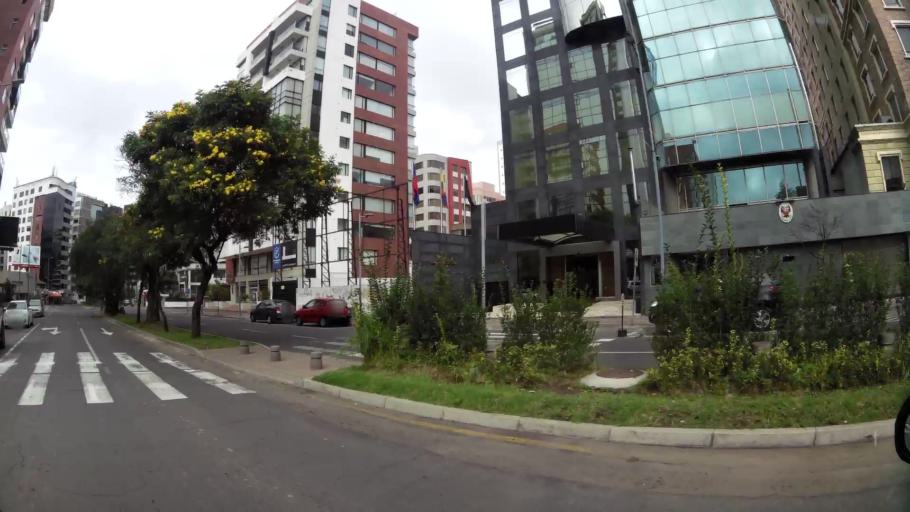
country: EC
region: Pichincha
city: Quito
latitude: -0.1837
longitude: -78.4806
